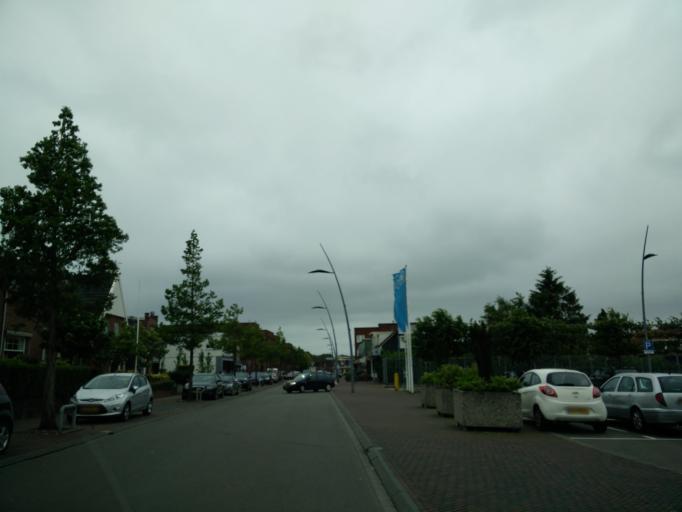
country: NL
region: Groningen
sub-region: Gemeente Zuidhorn
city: Aduard
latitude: 53.2149
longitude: 6.5014
